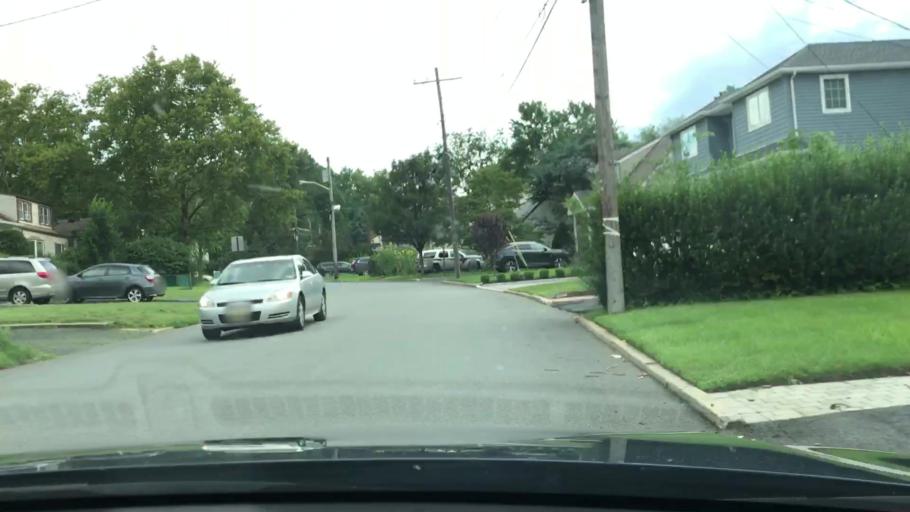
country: US
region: New Jersey
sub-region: Bergen County
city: Teaneck
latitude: 40.9161
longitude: -74.0155
